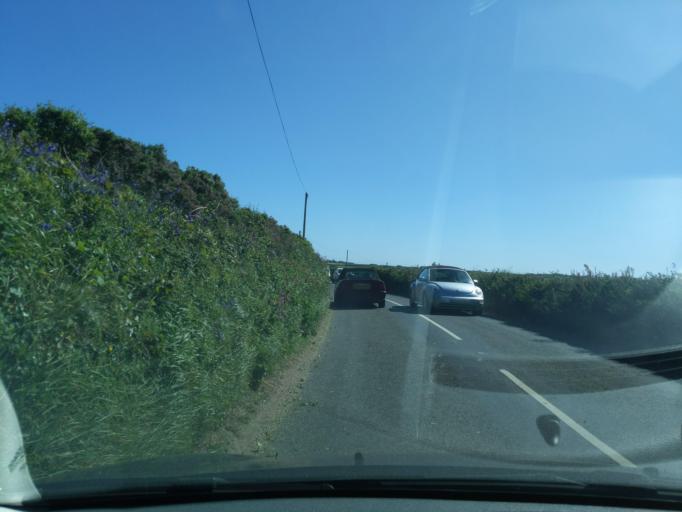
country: GB
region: England
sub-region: Cornwall
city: St. Buryan
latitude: 50.0864
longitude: -5.6036
